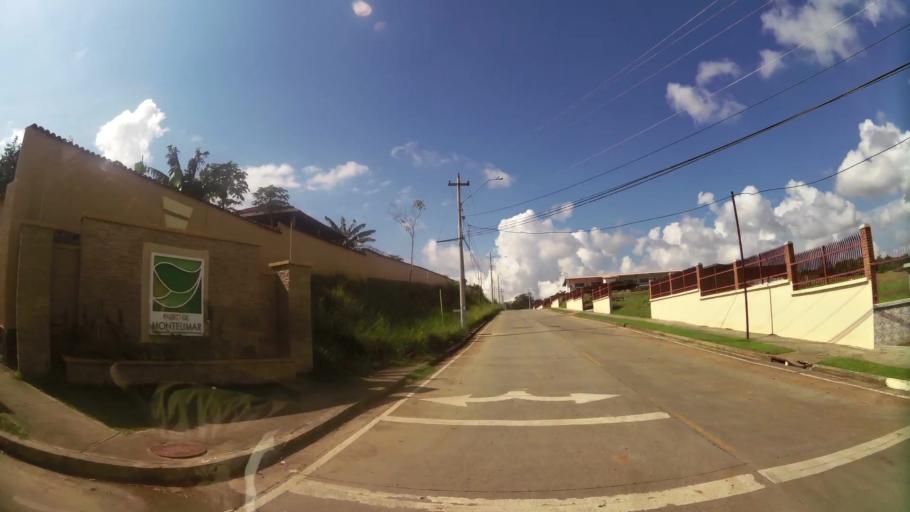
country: PA
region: Panama
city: Nuevo Arraijan
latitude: 8.9044
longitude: -79.7468
